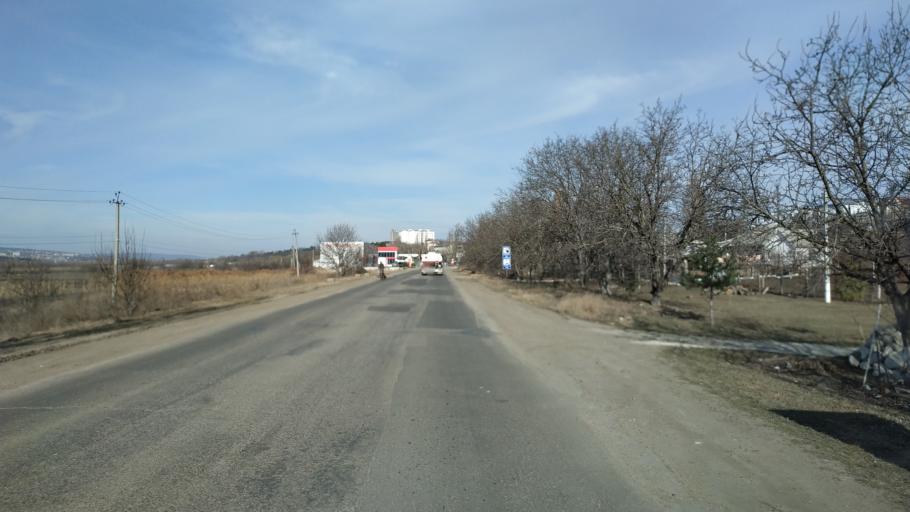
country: MD
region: Laloveni
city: Ialoveni
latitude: 46.9483
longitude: 28.7692
